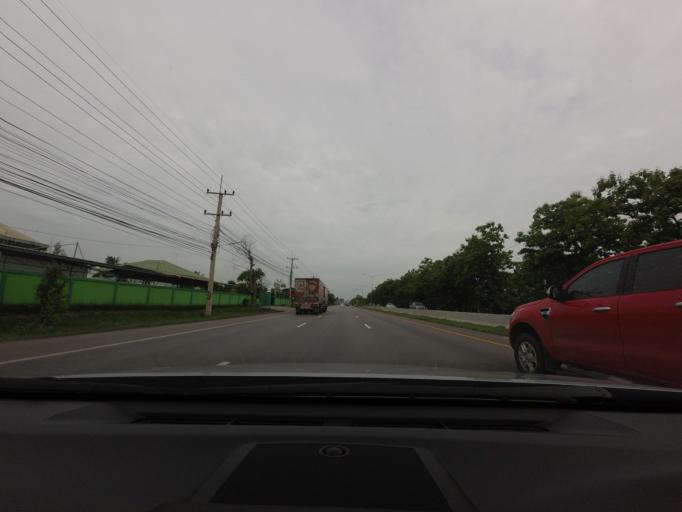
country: TH
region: Phetchaburi
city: Khao Yoi
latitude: 13.1570
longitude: 99.8479
